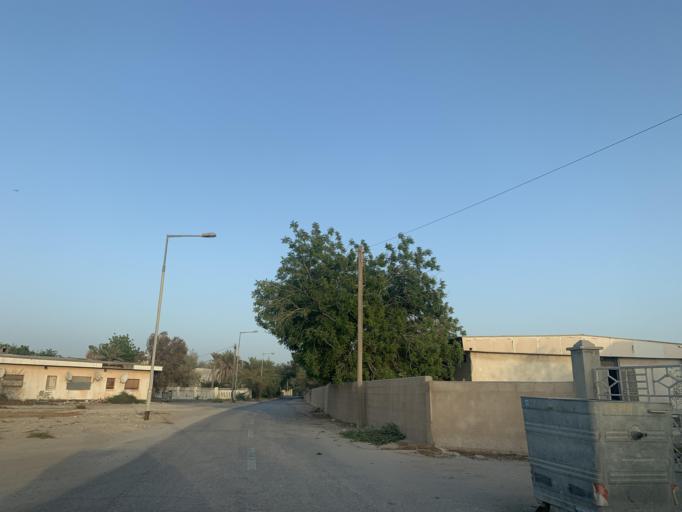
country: BH
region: Manama
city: Jidd Hafs
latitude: 26.2208
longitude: 50.5257
